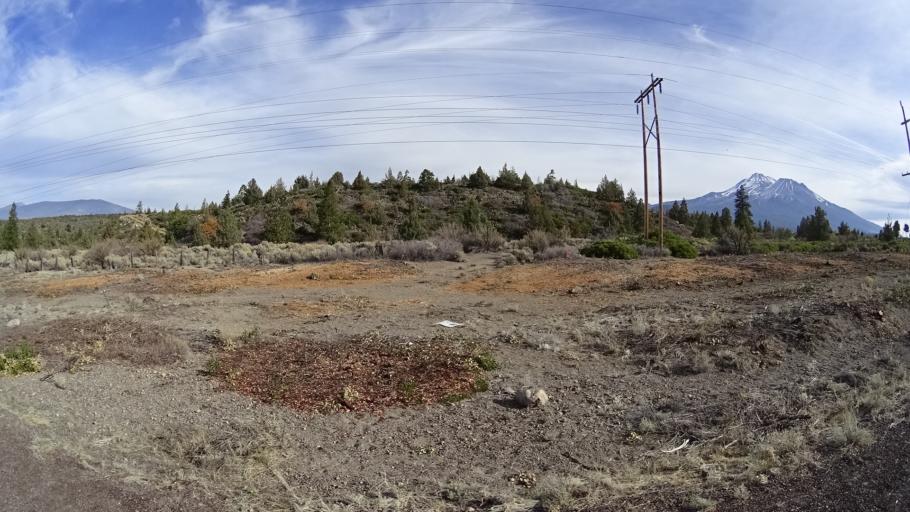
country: US
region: California
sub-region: Siskiyou County
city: Weed
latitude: 41.5008
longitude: -122.3633
